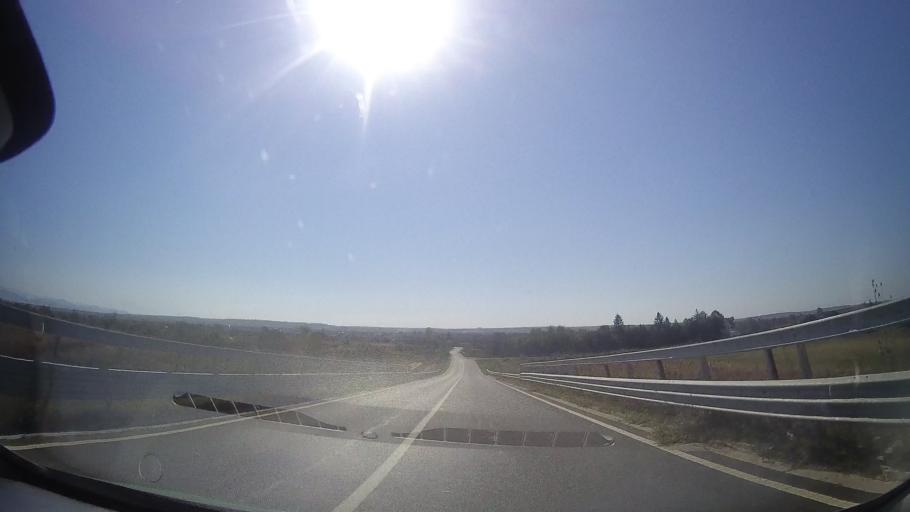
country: RO
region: Timis
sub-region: Comuna Bethausen
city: Bethausen
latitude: 45.8144
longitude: 21.9591
